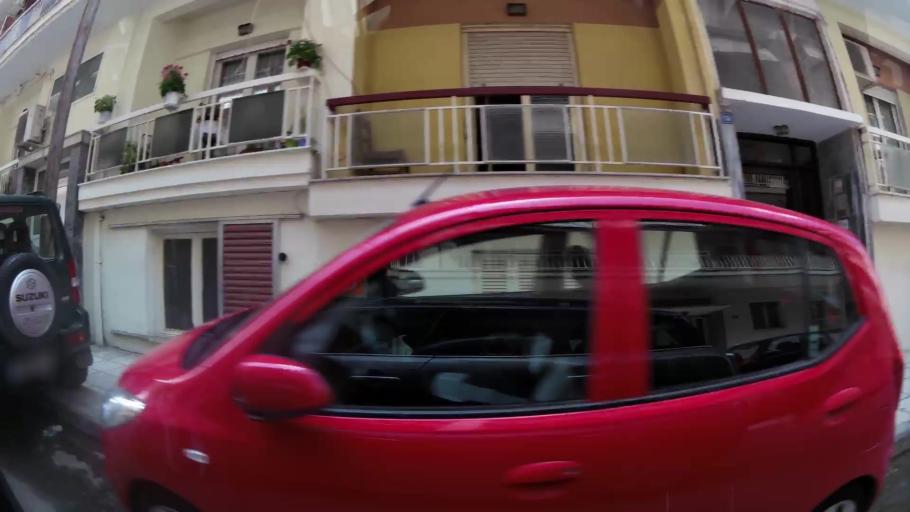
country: GR
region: Central Macedonia
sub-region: Nomos Imathias
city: Veroia
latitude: 40.5285
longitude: 22.2053
